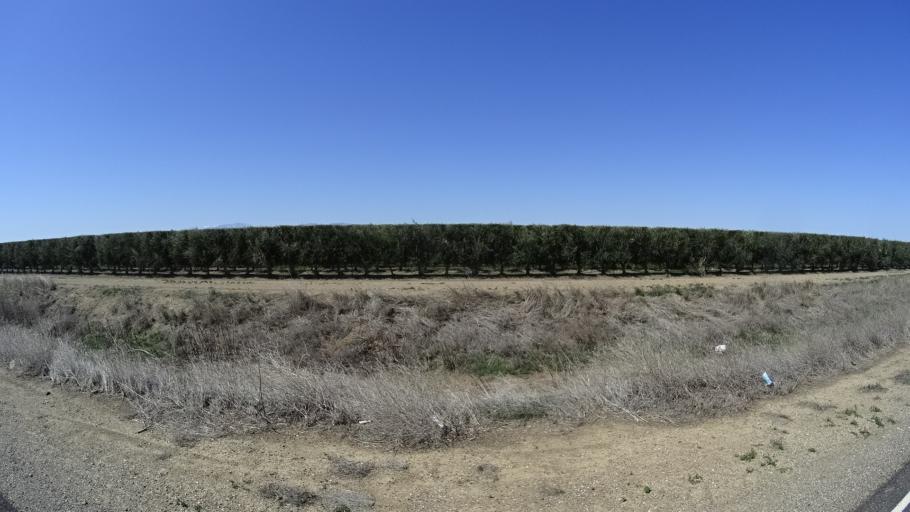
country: US
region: California
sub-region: Glenn County
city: Willows
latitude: 39.6000
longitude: -122.2498
